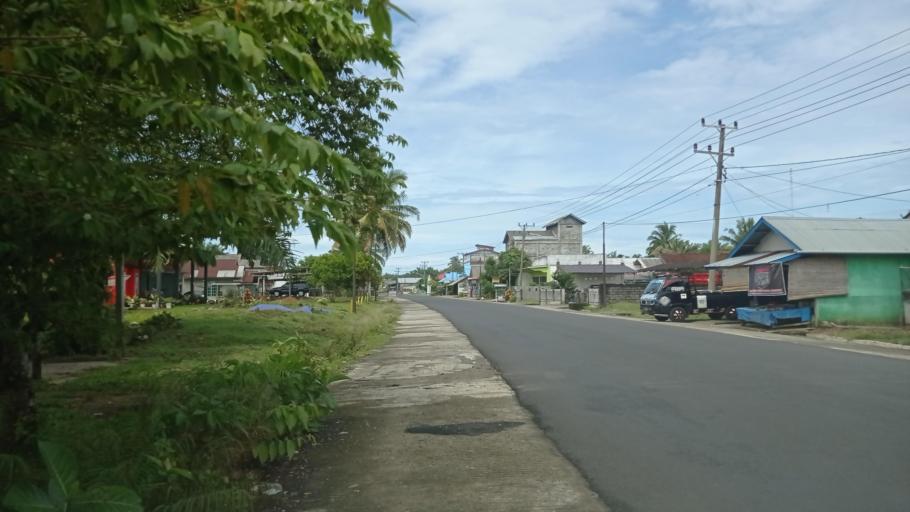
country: ID
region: Bengkulu
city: Ipuh
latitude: -2.5984
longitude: 101.1199
